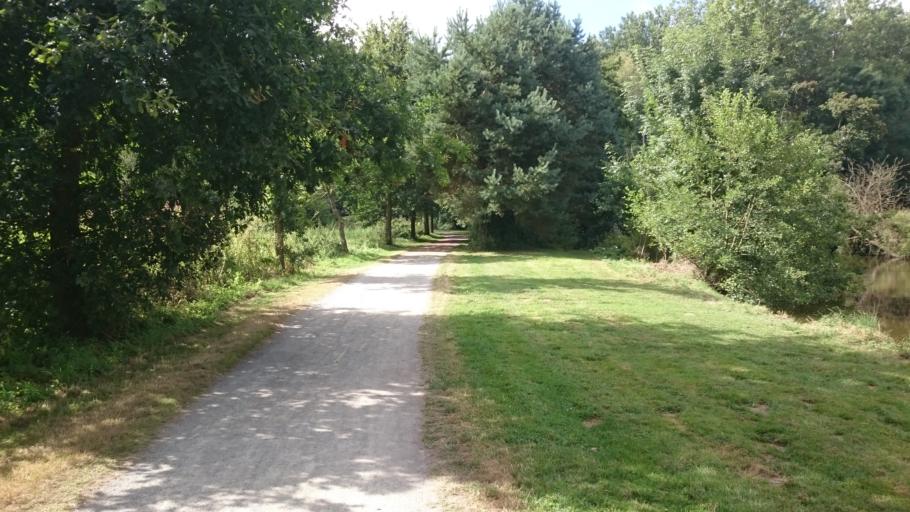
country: FR
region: Brittany
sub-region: Departement d'Ille-et-Vilaine
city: Vern-sur-Seiche
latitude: 48.0378
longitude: -1.6102
